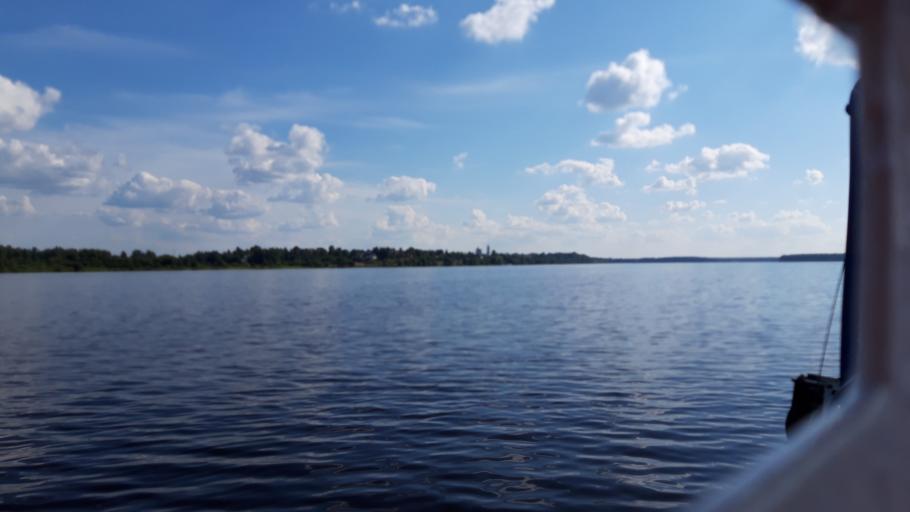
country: RU
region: Tverskaya
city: Zavidovo
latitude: 56.6464
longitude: 36.6202
